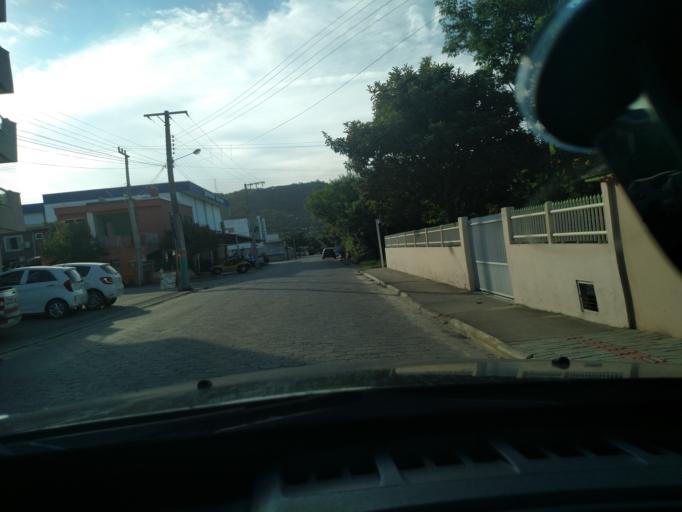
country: BR
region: Santa Catarina
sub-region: Porto Belo
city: Porto Belo
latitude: -27.1479
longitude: -48.5112
